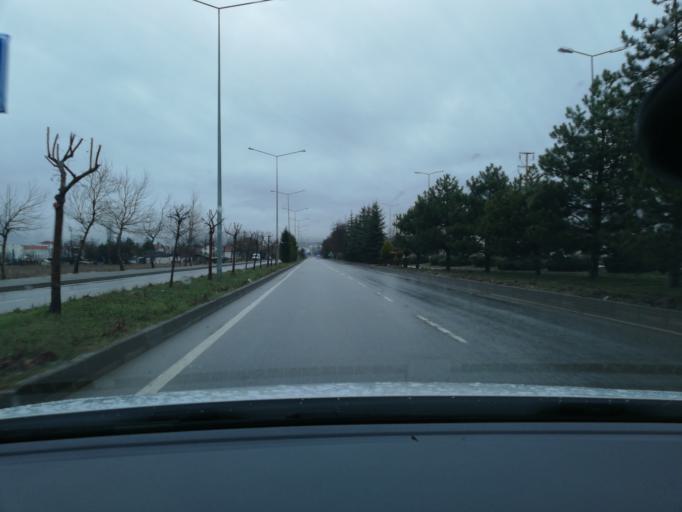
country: TR
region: Bolu
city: Bolu
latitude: 40.7191
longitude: 31.6139
